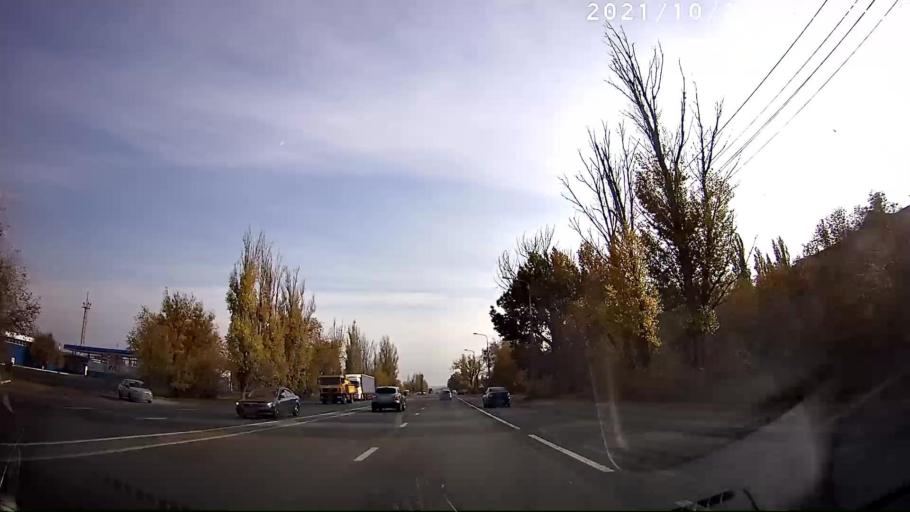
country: RU
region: Volgograd
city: Volgograd
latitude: 48.5654
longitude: 44.4342
